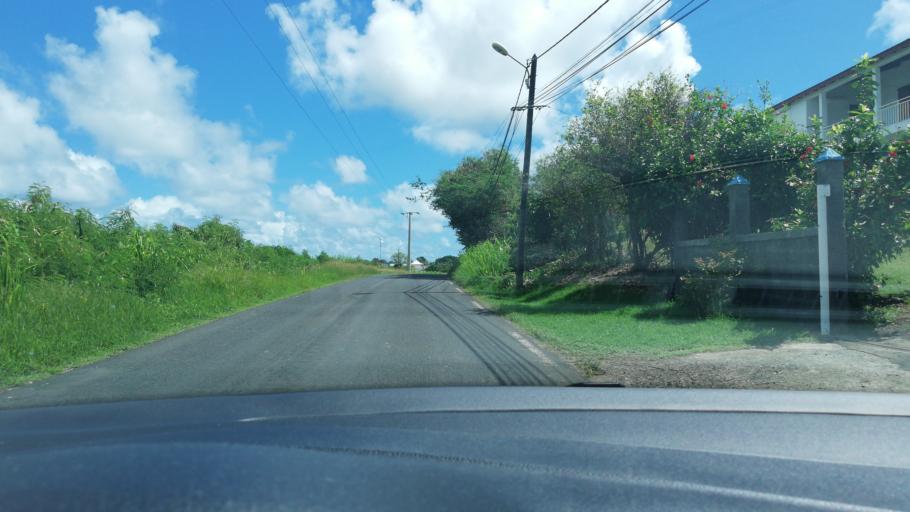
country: GP
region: Guadeloupe
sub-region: Guadeloupe
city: Petit-Canal
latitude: 16.3796
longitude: -61.4402
